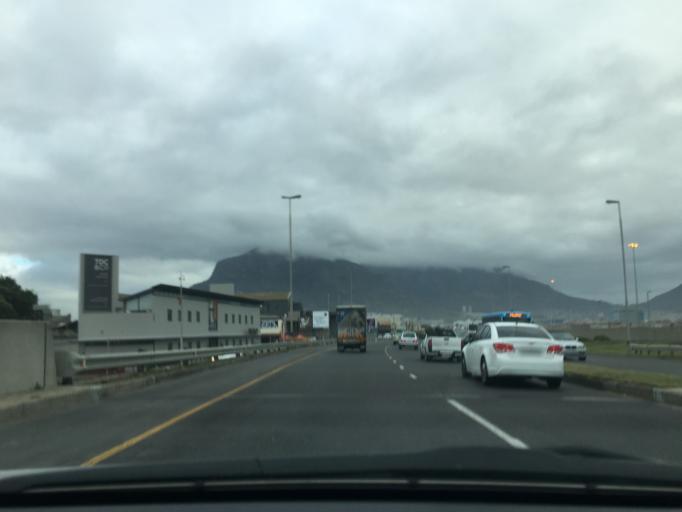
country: ZA
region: Western Cape
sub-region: City of Cape Town
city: Rosebank
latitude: -33.9085
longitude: 18.4728
